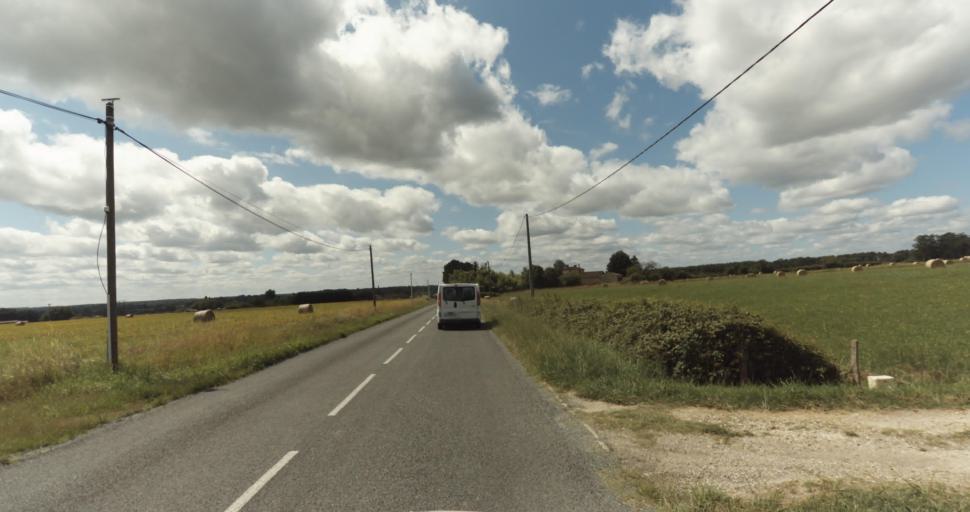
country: FR
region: Aquitaine
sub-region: Departement de la Gironde
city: Bazas
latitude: 44.4448
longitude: -0.2065
